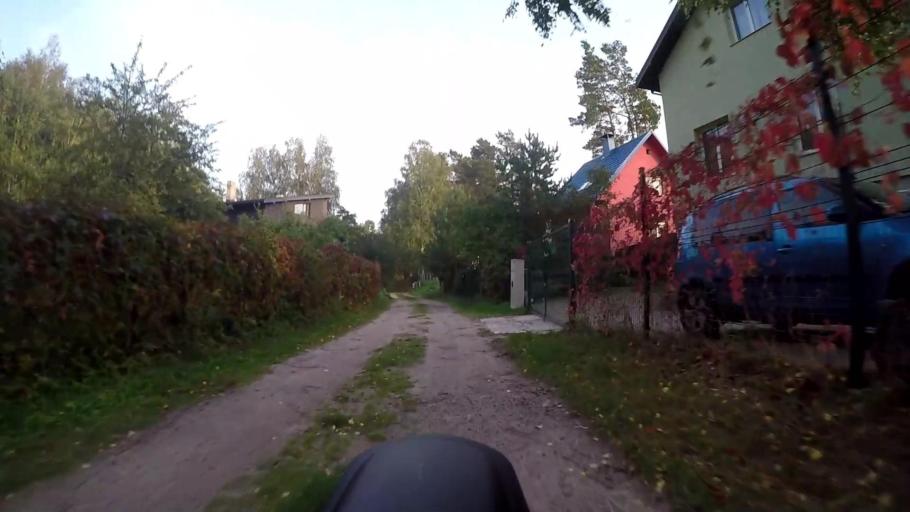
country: LV
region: Saulkrastu
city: Saulkrasti
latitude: 57.1888
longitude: 24.3544
